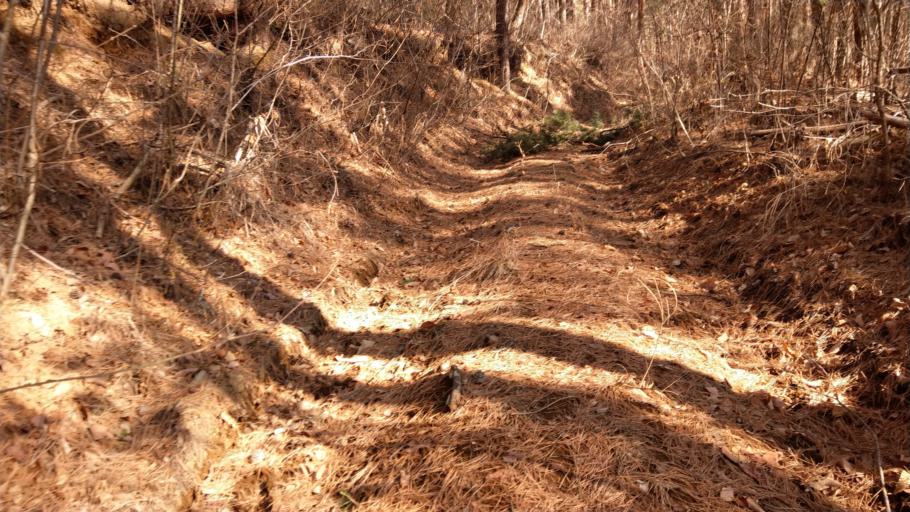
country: JP
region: Nagano
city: Komoro
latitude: 36.3674
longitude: 138.4334
